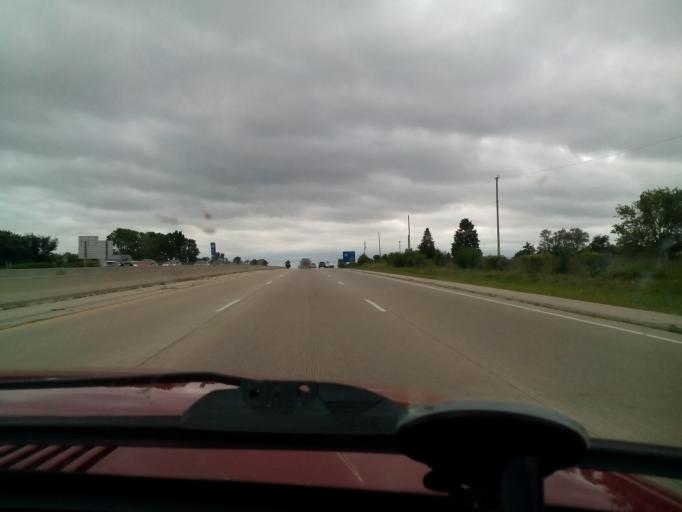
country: US
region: Wisconsin
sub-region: Dane County
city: Sun Prairie
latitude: 43.1551
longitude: -89.2747
